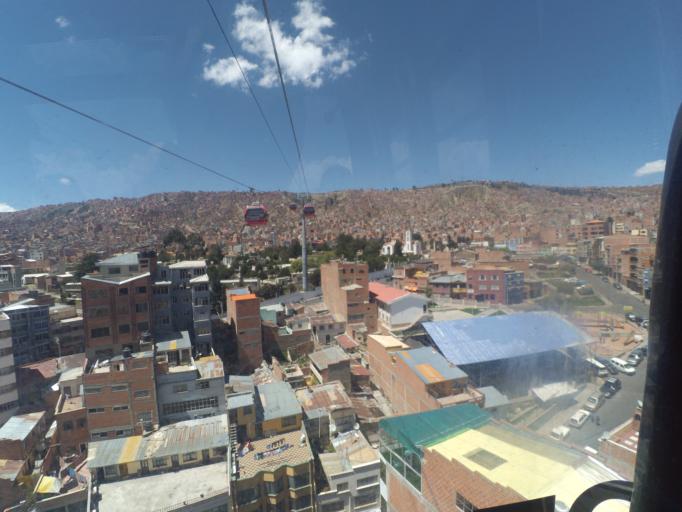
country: BO
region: La Paz
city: La Paz
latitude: -16.4951
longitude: -68.1491
